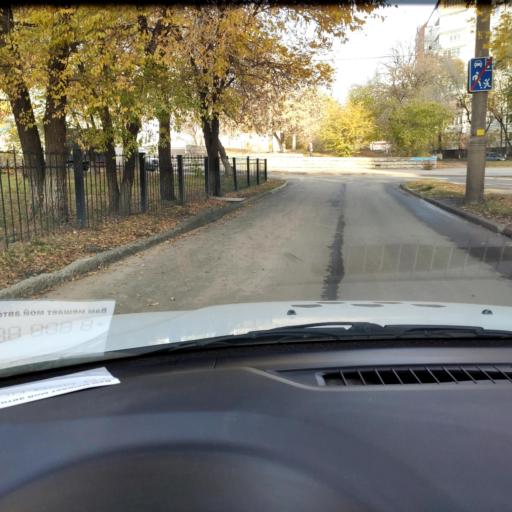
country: RU
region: Samara
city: Zhigulevsk
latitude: 53.4770
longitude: 49.4653
